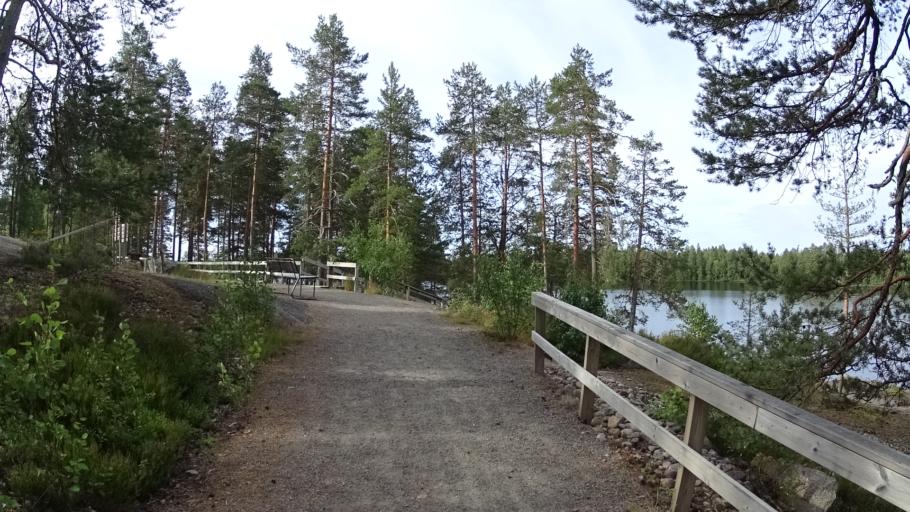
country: FI
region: Southern Ostrobothnia
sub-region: Kuusiokunnat
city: AEhtaeri
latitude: 62.5358
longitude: 24.1794
